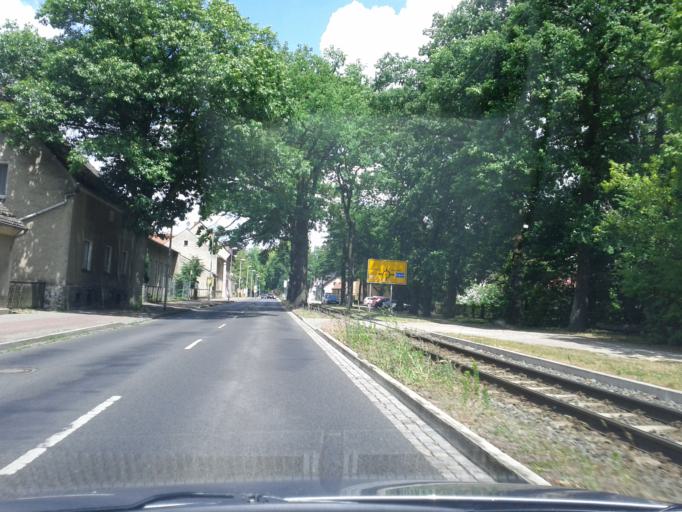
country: DE
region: Brandenburg
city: Schoneiche
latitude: 52.4775
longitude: 13.6943
